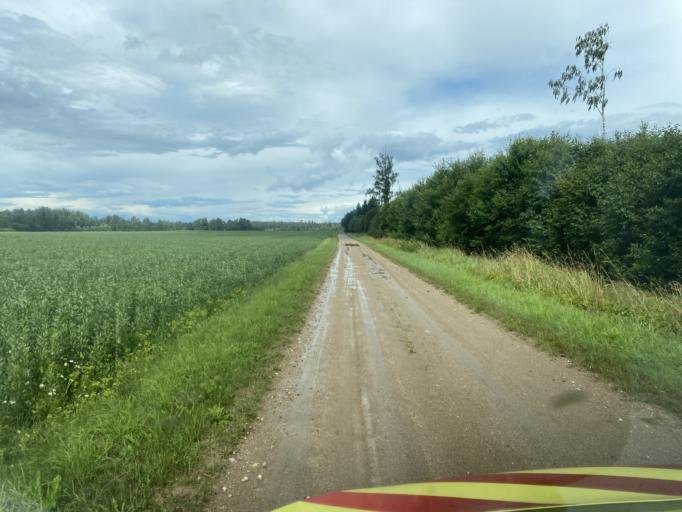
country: EE
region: Valgamaa
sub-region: Torva linn
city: Torva
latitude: 58.0999
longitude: 26.0024
